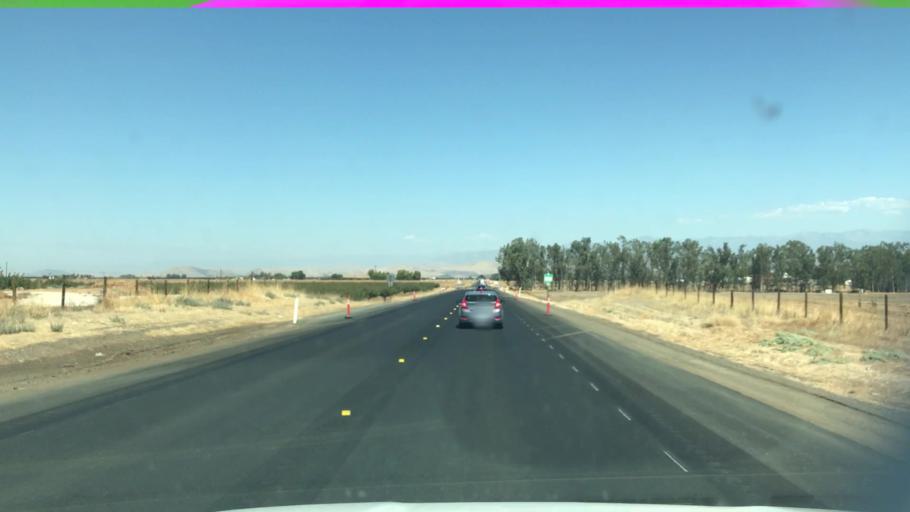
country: US
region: California
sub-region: Tulare County
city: Terra Bella
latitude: 35.9887
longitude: -119.0498
